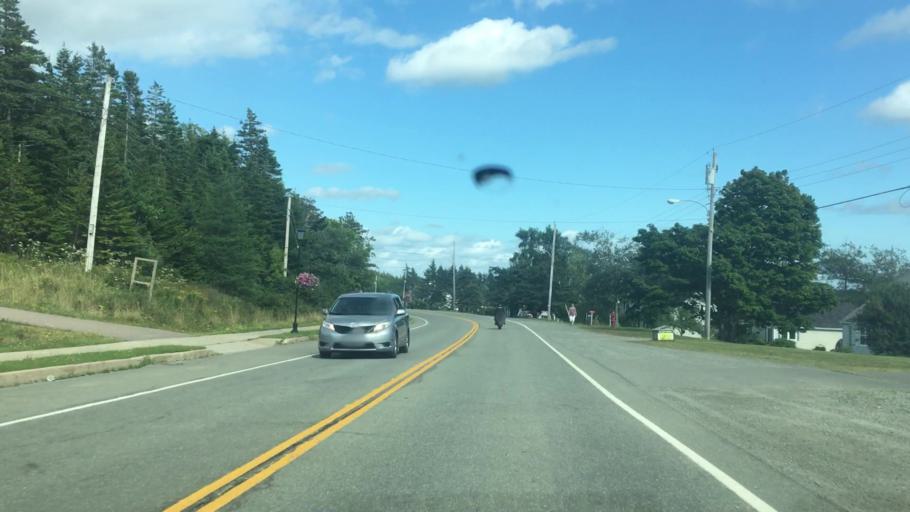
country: CA
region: Nova Scotia
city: Princeville
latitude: 45.6543
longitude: -60.8912
